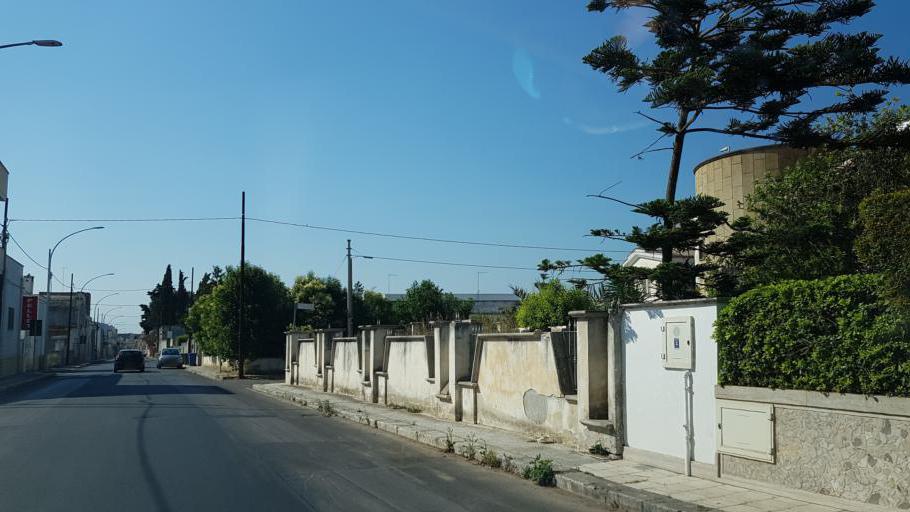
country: IT
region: Apulia
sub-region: Provincia di Brindisi
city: San Donaci
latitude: 40.4529
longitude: 17.9177
